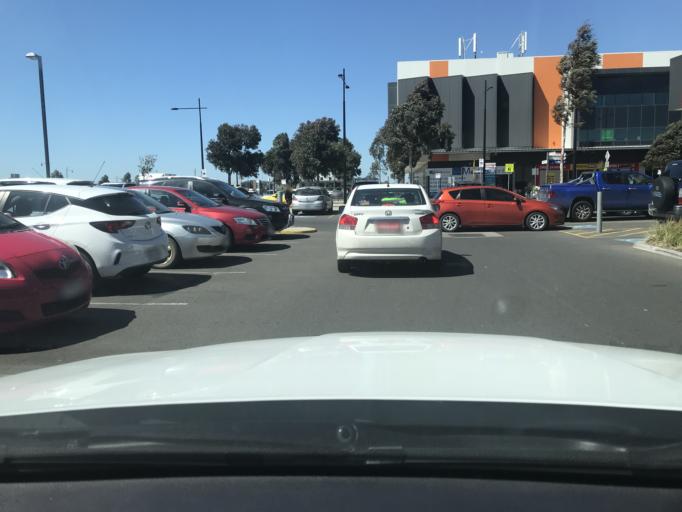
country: AU
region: Victoria
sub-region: Hume
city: Roxburgh Park
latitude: -37.5917
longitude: 144.9139
